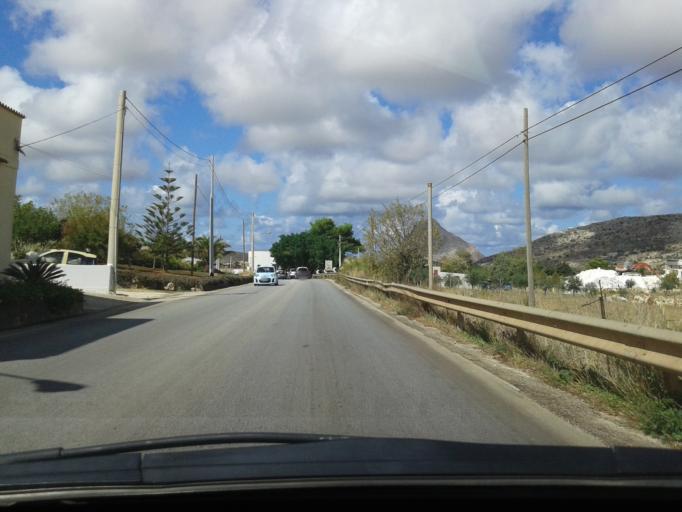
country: IT
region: Sicily
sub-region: Trapani
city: Castelluzzo
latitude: 38.0781
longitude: 12.7259
